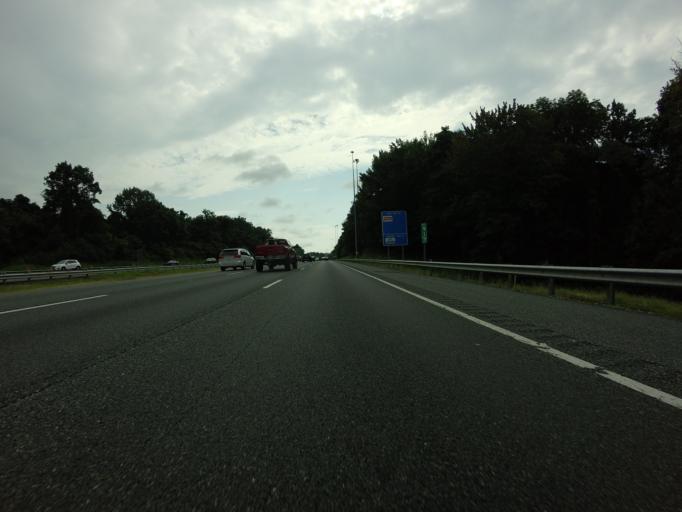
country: US
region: Maryland
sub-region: Cecil County
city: Perryville
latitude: 39.5855
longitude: -76.0896
